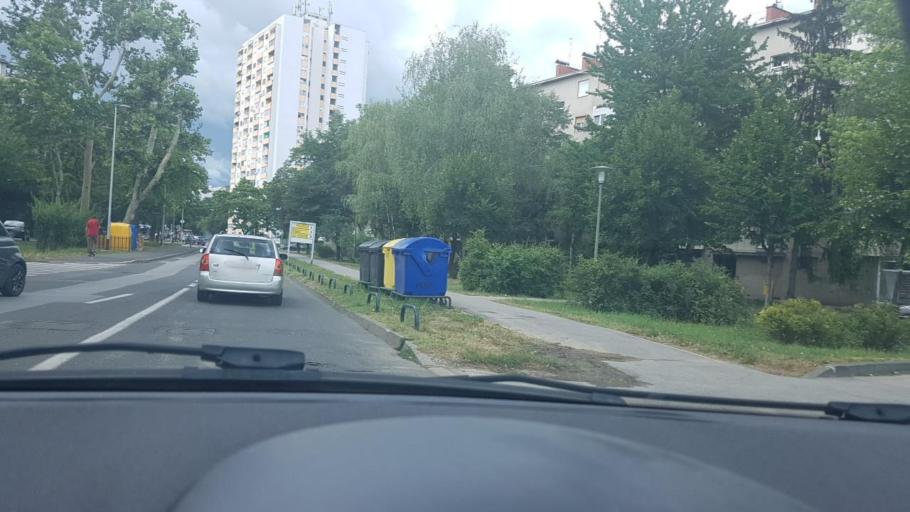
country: HR
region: Grad Zagreb
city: Novi Zagreb
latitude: 45.8044
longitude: 16.0201
